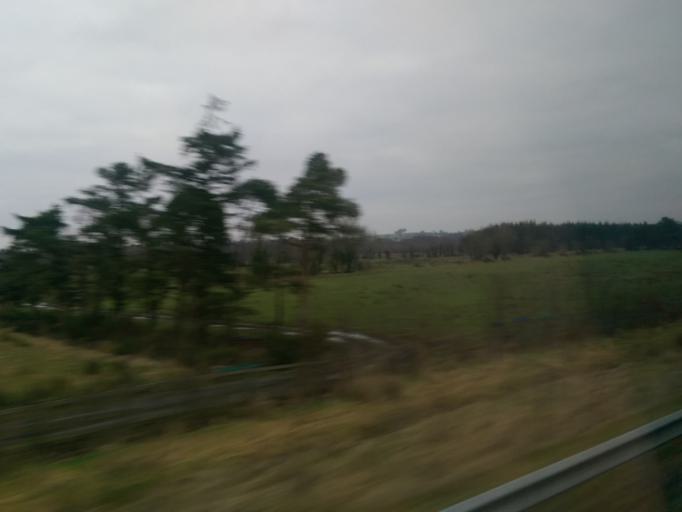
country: IE
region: Connaught
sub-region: County Galway
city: Ballinasloe
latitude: 53.3081
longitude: -8.3135
